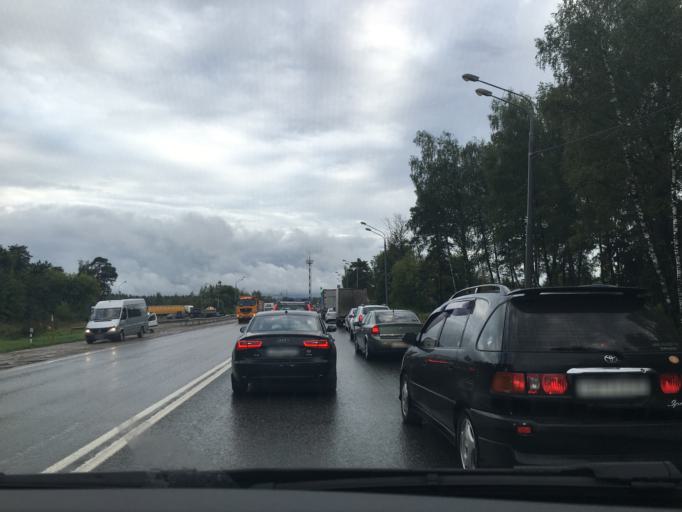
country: RU
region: Kaluga
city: Obninsk
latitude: 55.0802
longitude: 36.6297
